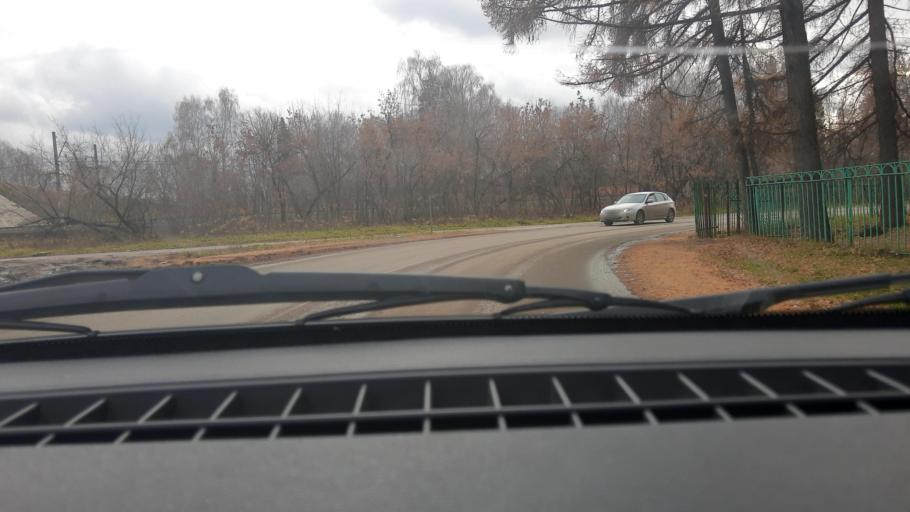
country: RU
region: Bashkortostan
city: Iglino
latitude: 54.8323
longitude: 56.4229
